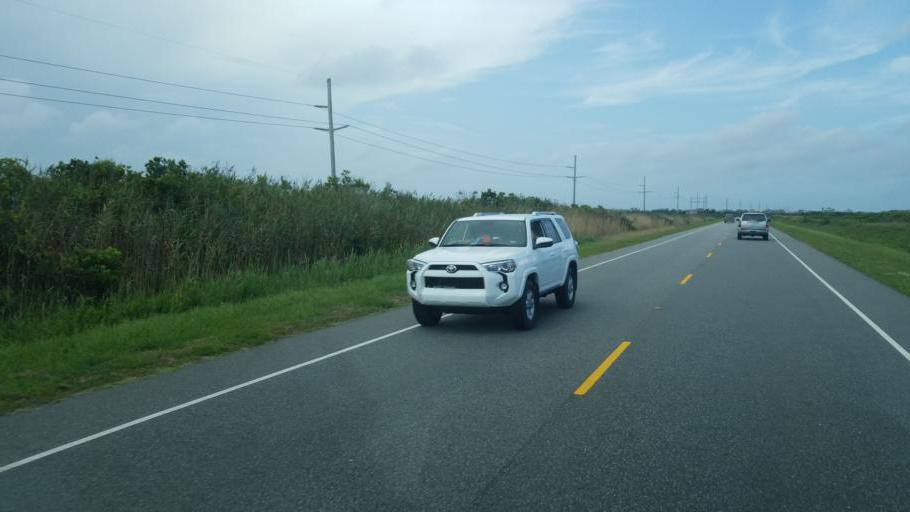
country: US
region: North Carolina
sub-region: Dare County
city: Buxton
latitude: 35.3104
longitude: -75.5115
